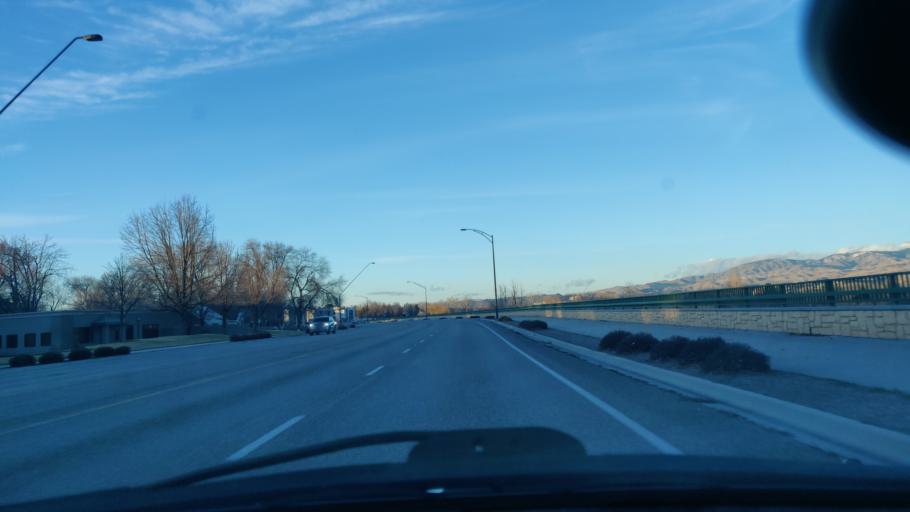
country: US
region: Idaho
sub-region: Ada County
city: Boise
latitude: 43.5802
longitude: -116.1984
